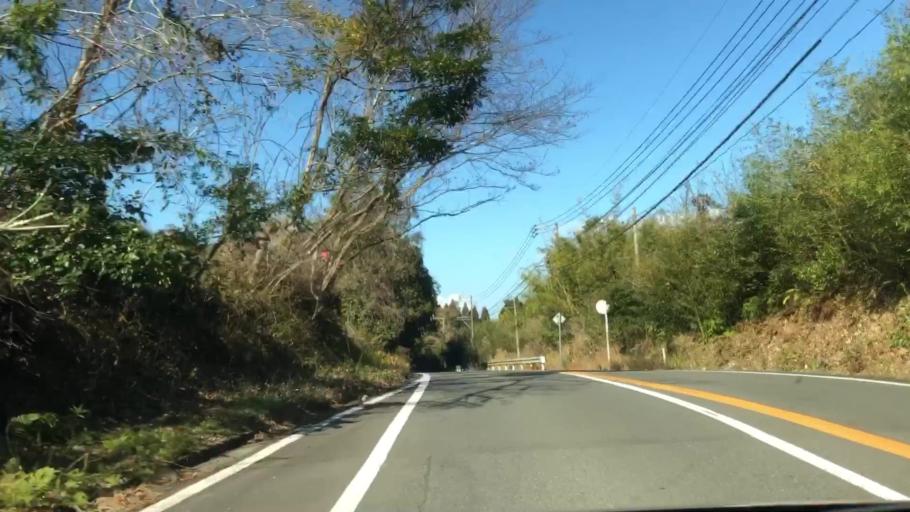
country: JP
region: Kagoshima
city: Satsumasendai
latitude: 31.8538
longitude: 130.4293
